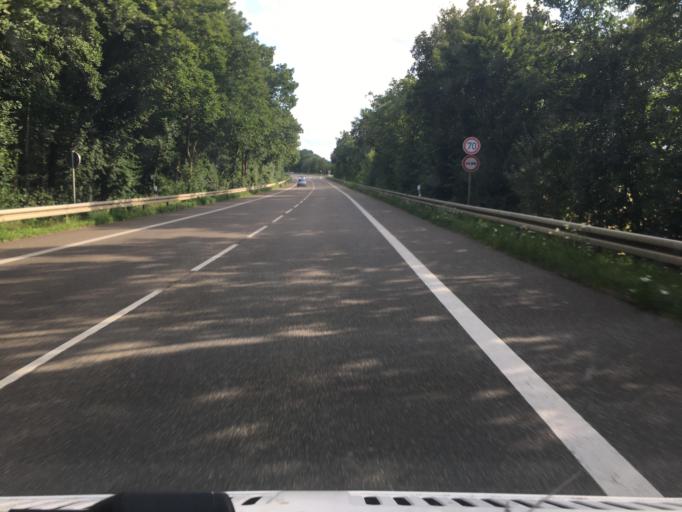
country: DE
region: North Rhine-Westphalia
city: Zulpich
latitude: 50.7105
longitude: 6.6478
